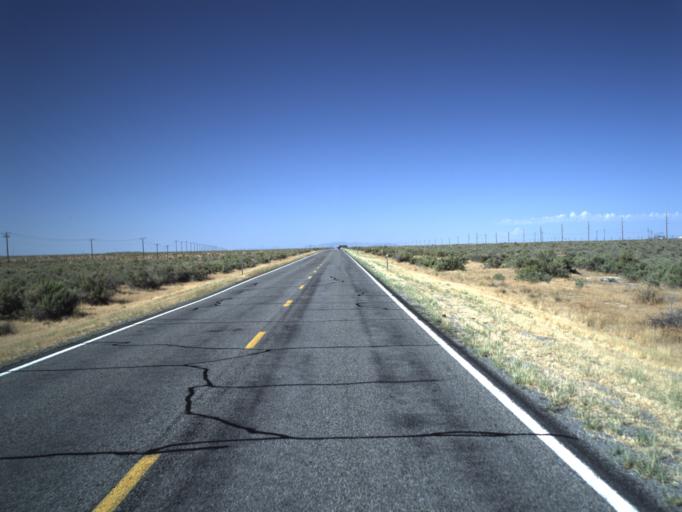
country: US
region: Utah
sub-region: Millard County
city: Delta
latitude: 39.4743
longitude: -112.4200
